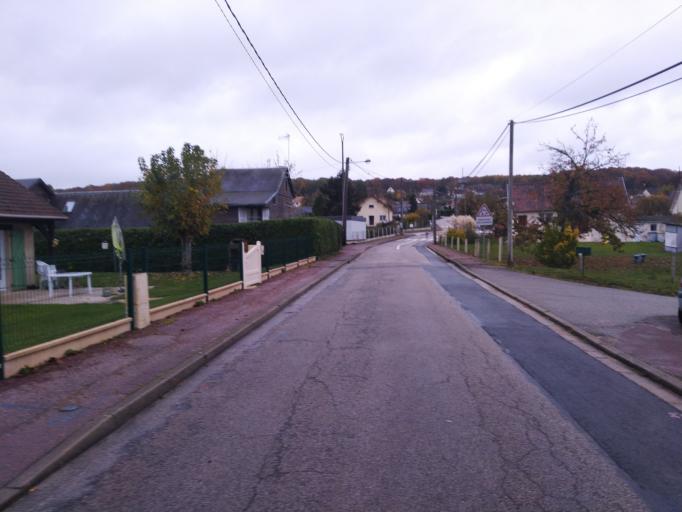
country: FR
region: Haute-Normandie
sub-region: Departement de la Seine-Maritime
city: Yainville
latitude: 49.4591
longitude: 0.8332
